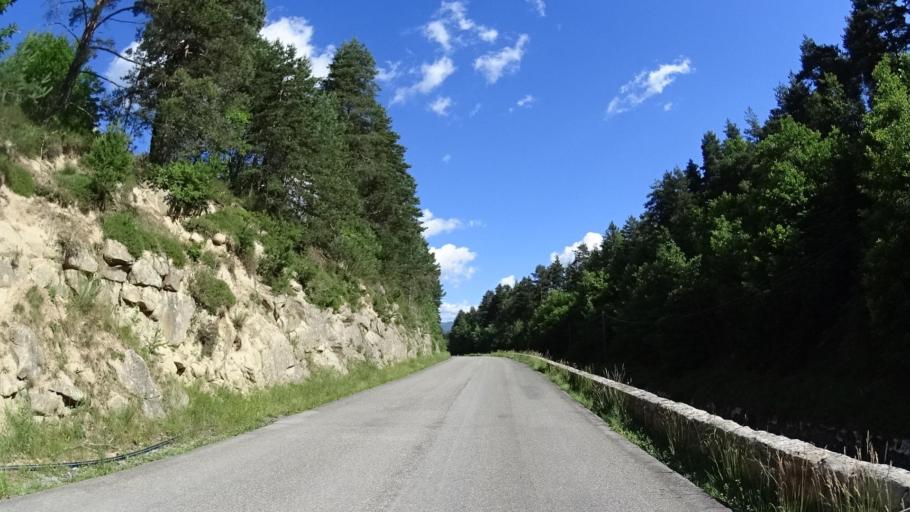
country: FR
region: Provence-Alpes-Cote d'Azur
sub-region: Departement des Alpes-de-Haute-Provence
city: Annot
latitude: 43.9826
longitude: 6.6501
